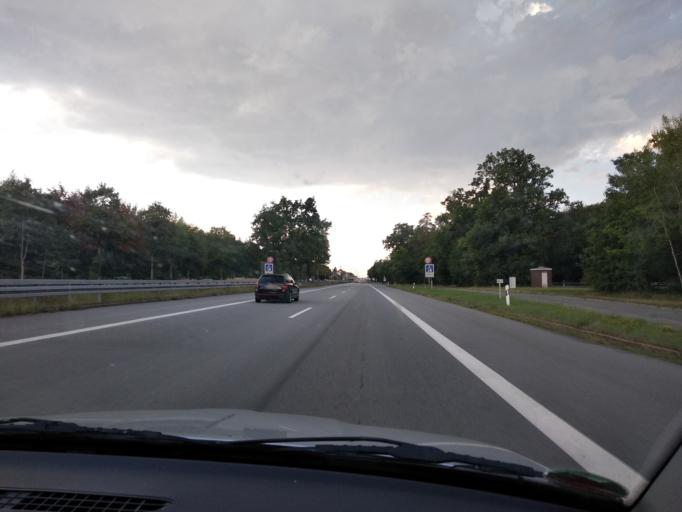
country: DE
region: Bavaria
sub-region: Upper Bavaria
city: Unterhaching
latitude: 48.0905
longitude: 11.5910
